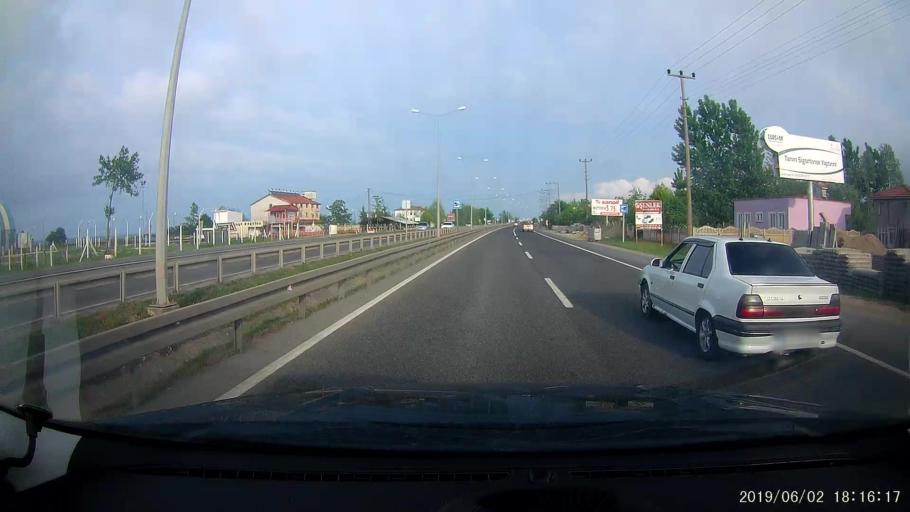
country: TR
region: Ordu
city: Unieh
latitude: 41.1019
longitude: 37.3957
